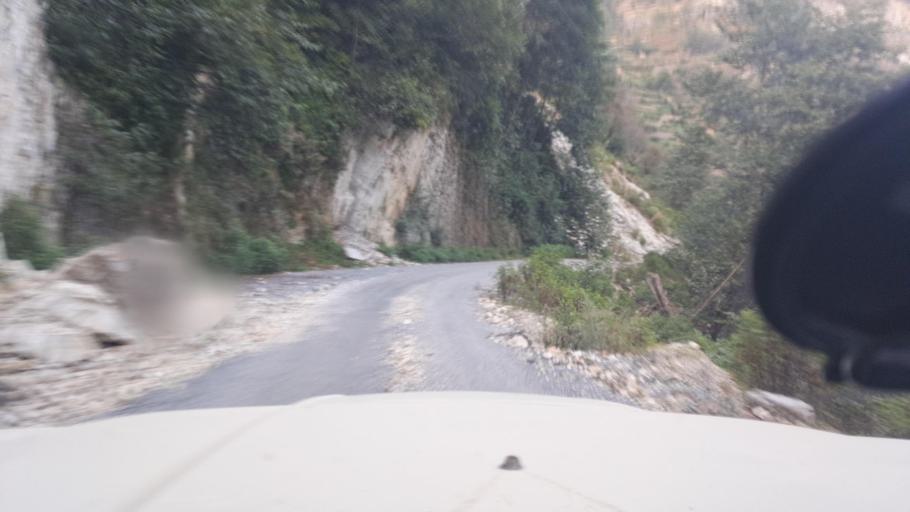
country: NP
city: Besisahar
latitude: 28.5910
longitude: 82.5705
